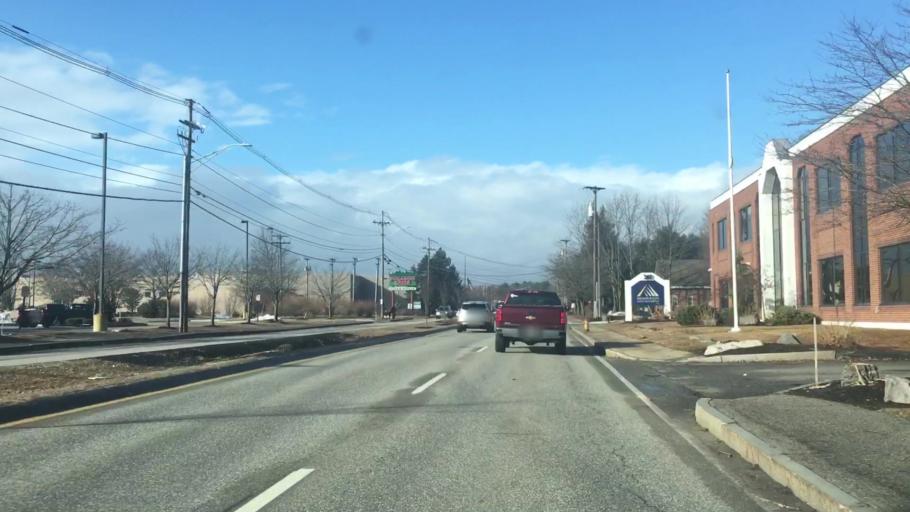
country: US
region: Maine
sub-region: Cumberland County
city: South Portland Gardens
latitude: 43.6341
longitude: -70.3259
